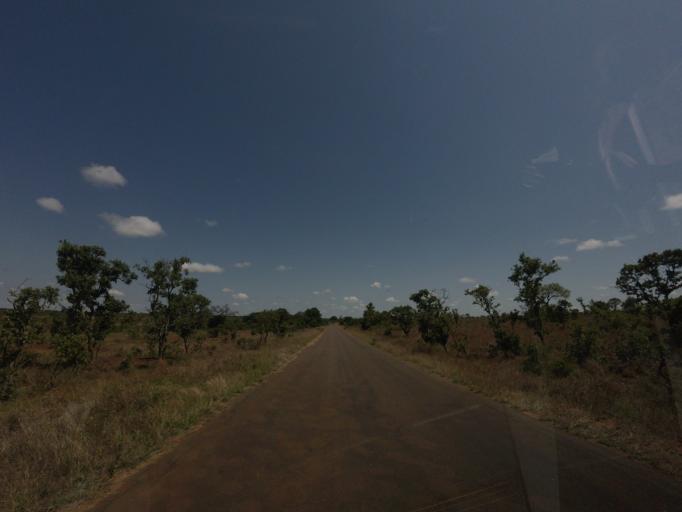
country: ZA
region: Mpumalanga
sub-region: Ehlanzeni District
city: Komatipoort
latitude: -24.9810
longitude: 31.9053
